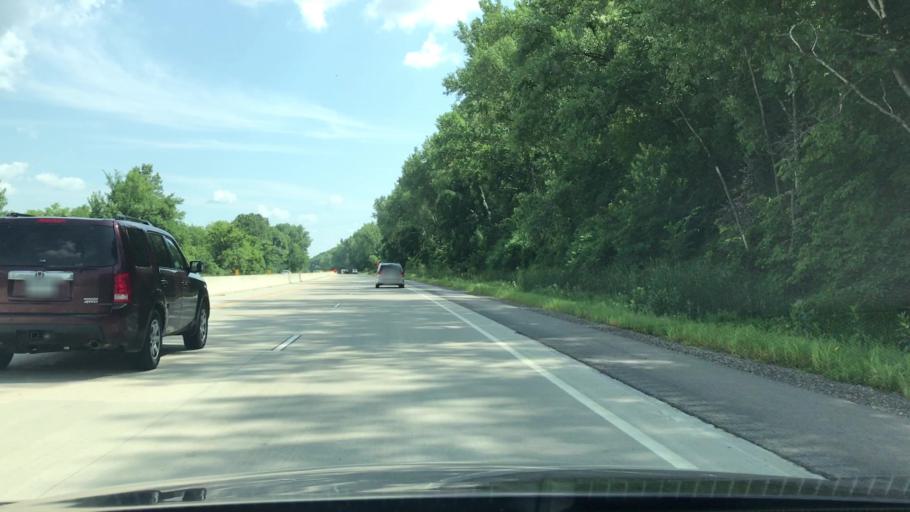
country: US
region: Minnesota
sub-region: Nicollet County
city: North Mankato
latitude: 44.2136
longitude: -94.0271
